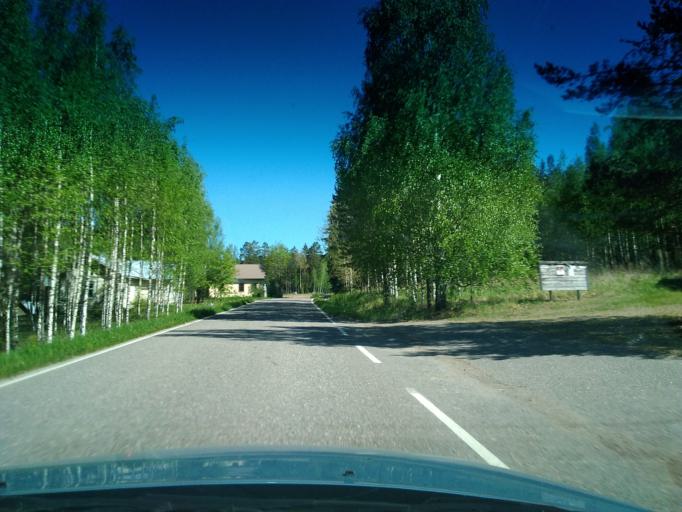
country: FI
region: Uusimaa
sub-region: Helsinki
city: Kaerkoelae
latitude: 60.6718
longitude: 23.9590
